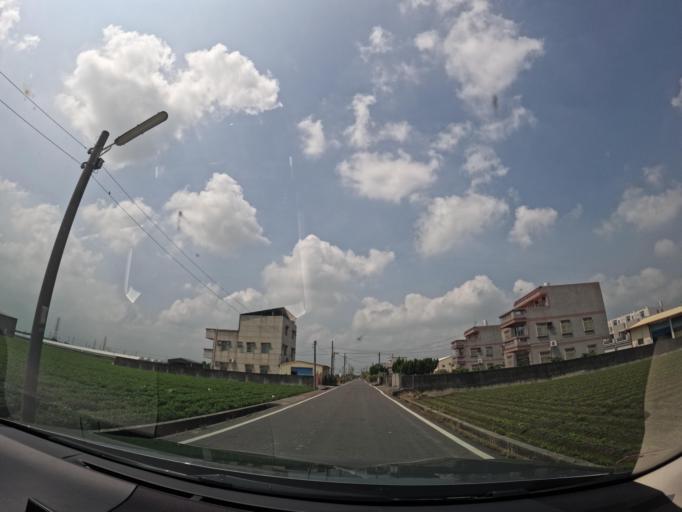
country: TW
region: Taiwan
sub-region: Yunlin
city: Douliu
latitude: 23.6644
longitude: 120.3941
